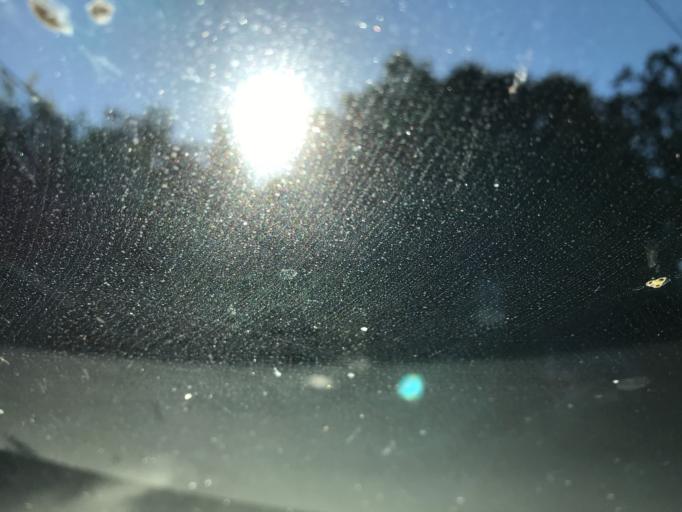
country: US
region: California
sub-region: San Mateo County
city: Menlo Park
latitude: 37.4628
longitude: -122.1644
